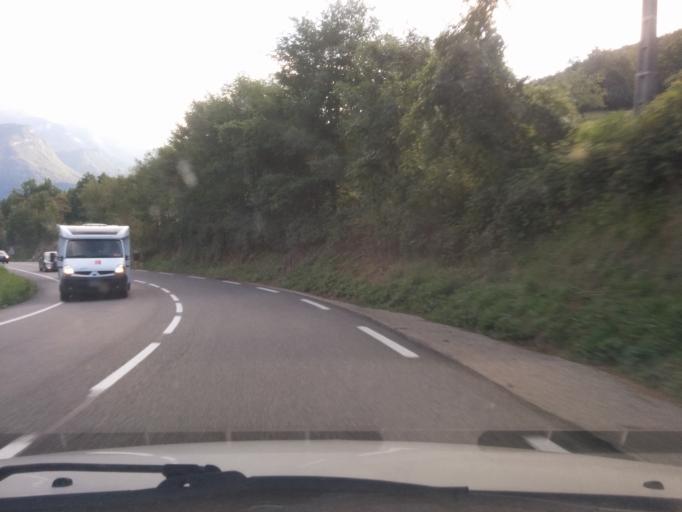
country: FR
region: Rhone-Alpes
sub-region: Departement de l'Isere
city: Voreppe
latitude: 45.3079
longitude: 5.6378
